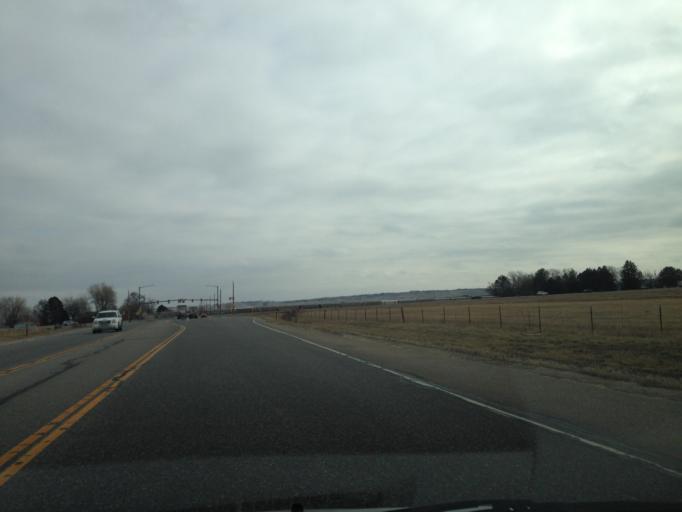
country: US
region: Colorado
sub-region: Boulder County
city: Louisville
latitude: 39.9578
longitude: -105.1314
